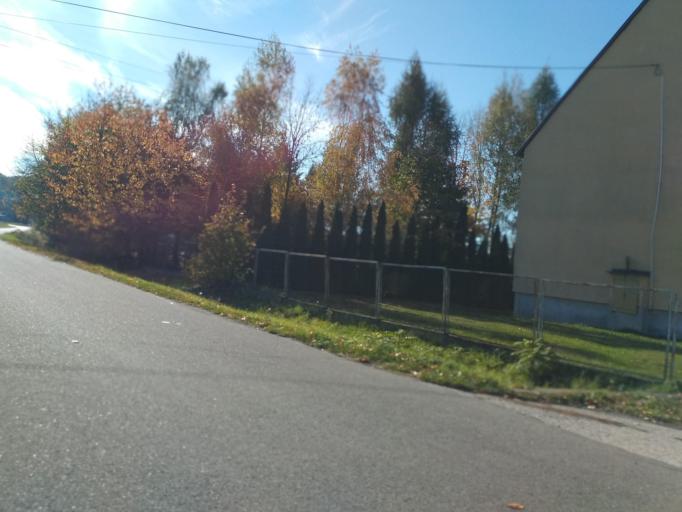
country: PL
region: Subcarpathian Voivodeship
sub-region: Powiat ropczycko-sedziszowski
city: Iwierzyce
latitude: 50.0595
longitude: 21.7862
